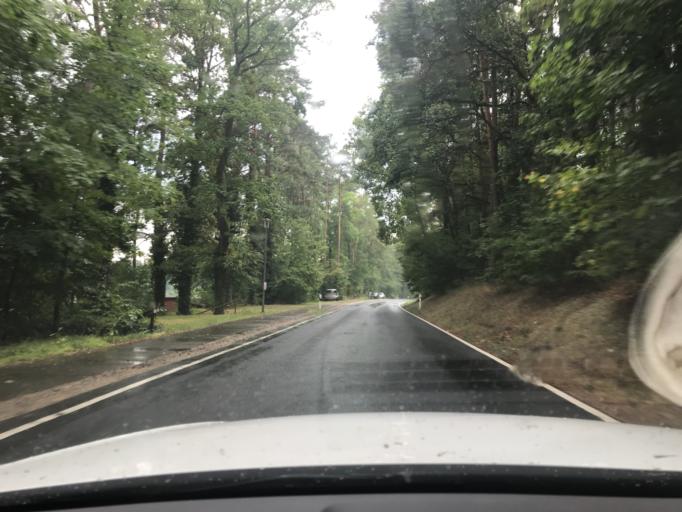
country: DE
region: Bavaria
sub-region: Upper Palatinate
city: Speinshart
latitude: 49.7586
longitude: 11.8032
